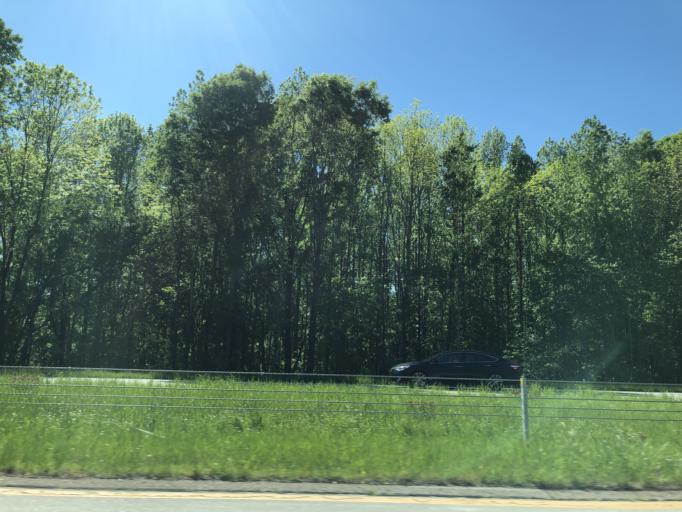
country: US
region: Georgia
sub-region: Oconee County
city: Bogart
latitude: 33.9312
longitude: -83.4673
